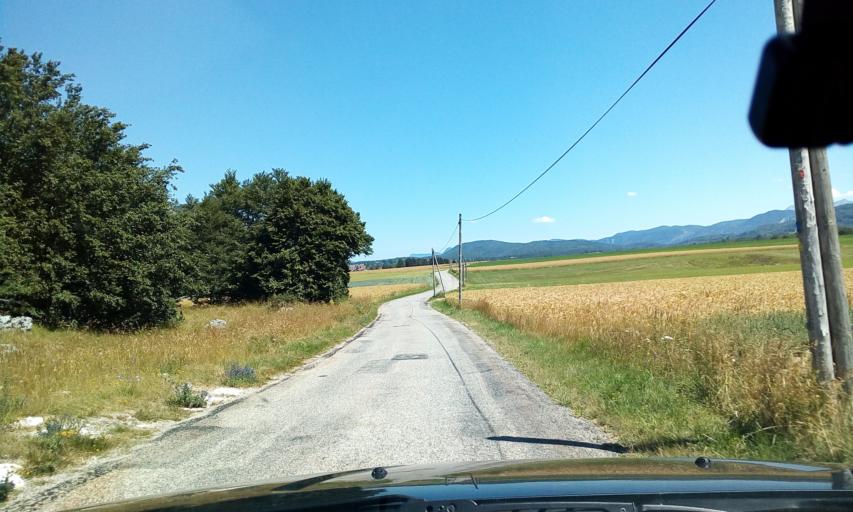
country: FR
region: Rhone-Alpes
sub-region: Departement de la Drome
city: Die
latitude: 44.8837
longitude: 5.3666
